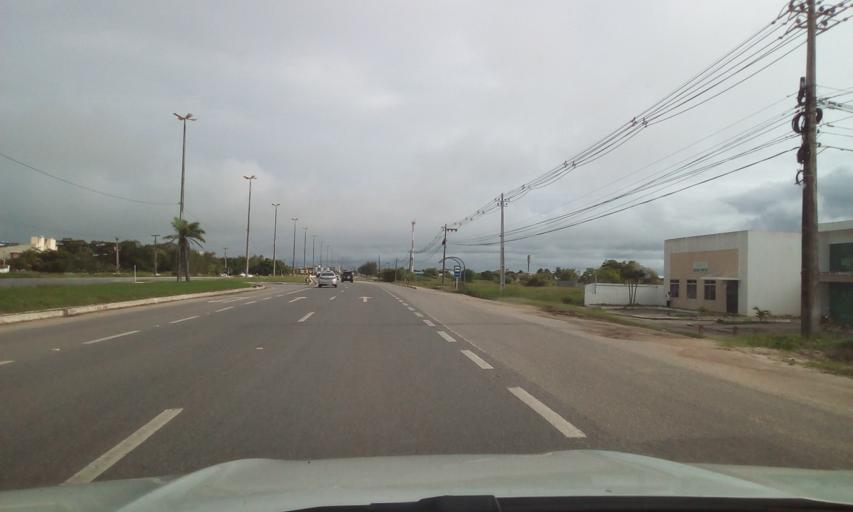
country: BR
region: Paraiba
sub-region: Cabedelo
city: Cabedelo
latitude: -7.0121
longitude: -34.8323
